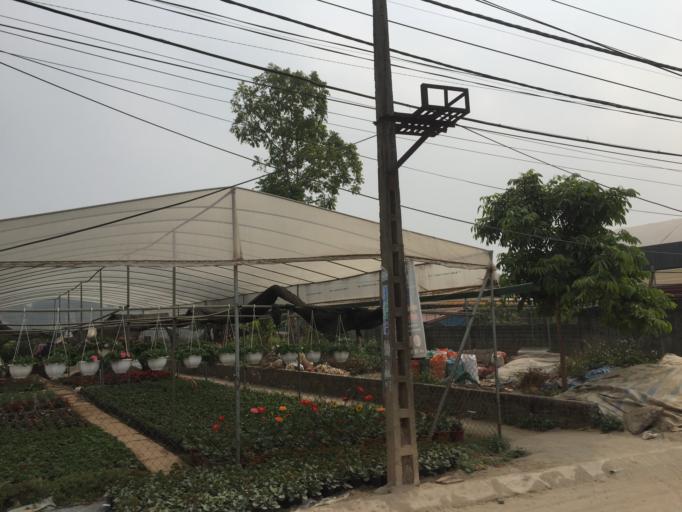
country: VN
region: Hung Yen
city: Van Giang
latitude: 20.9589
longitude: 105.9103
